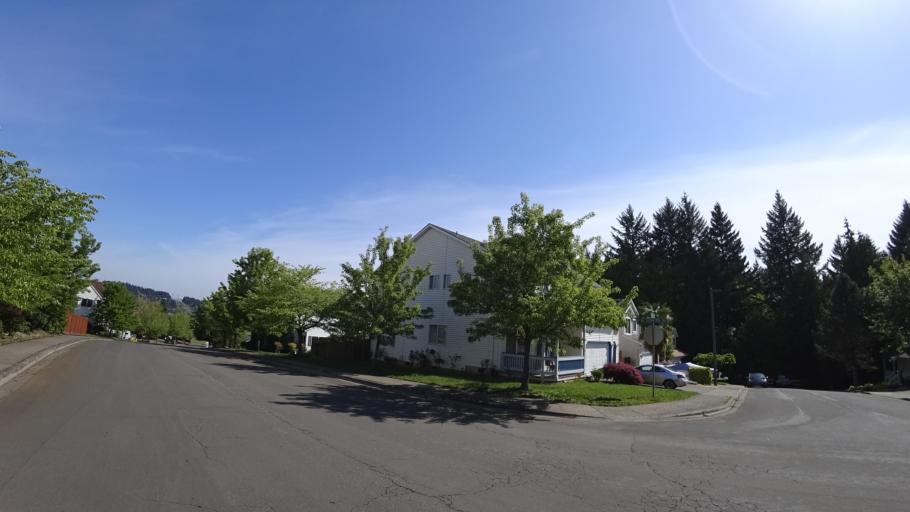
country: US
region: Oregon
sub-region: Washington County
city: Aloha
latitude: 45.4548
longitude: -122.8441
